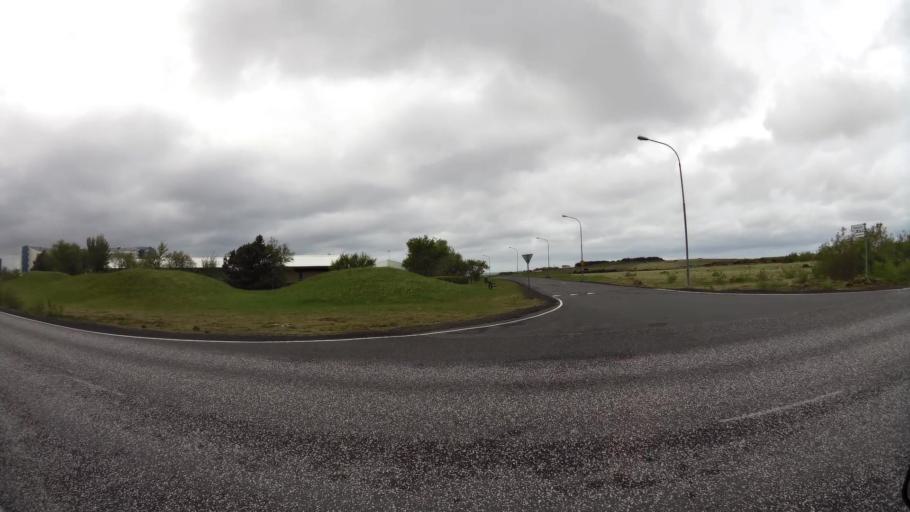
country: IS
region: Capital Region
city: Hafnarfjoerdur
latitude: 64.0816
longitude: -21.9695
